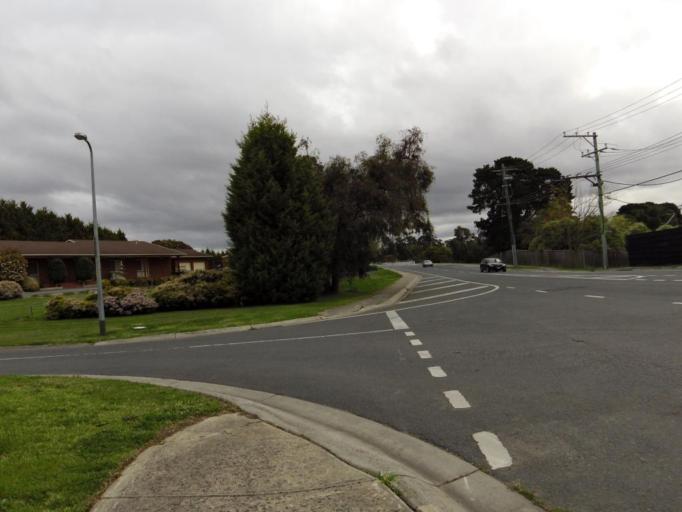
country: AU
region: Victoria
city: Mitcham
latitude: -37.7989
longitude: 145.1940
